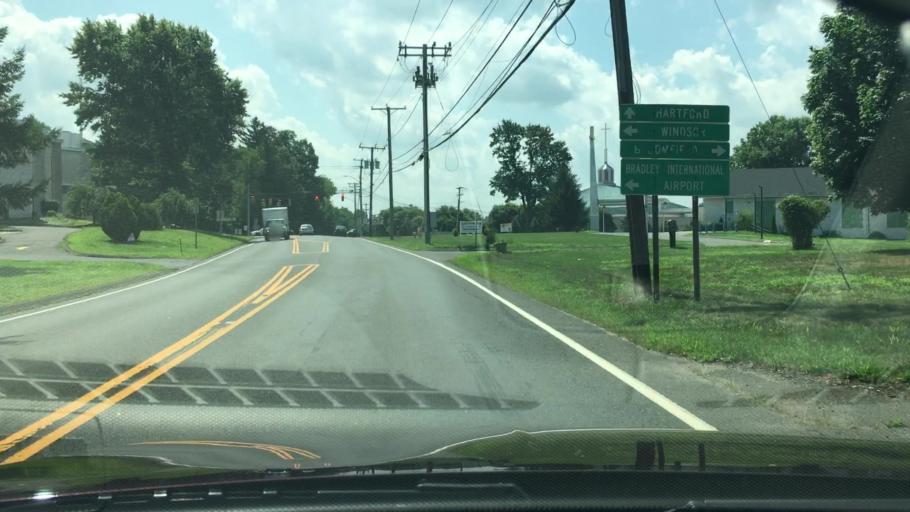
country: US
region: Connecticut
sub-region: Hartford County
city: Blue Hills
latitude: 41.8365
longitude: -72.6993
